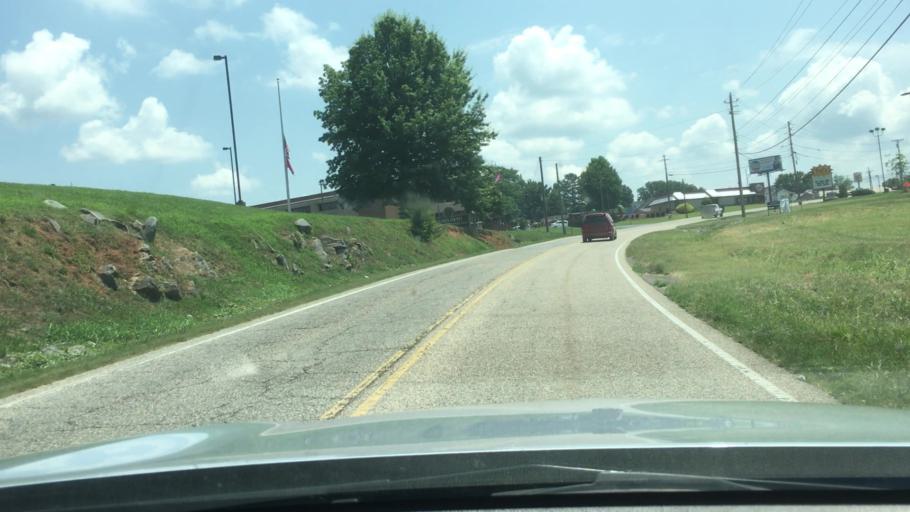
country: US
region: Tennessee
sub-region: Sullivan County
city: Blountville
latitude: 36.5357
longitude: -82.3228
